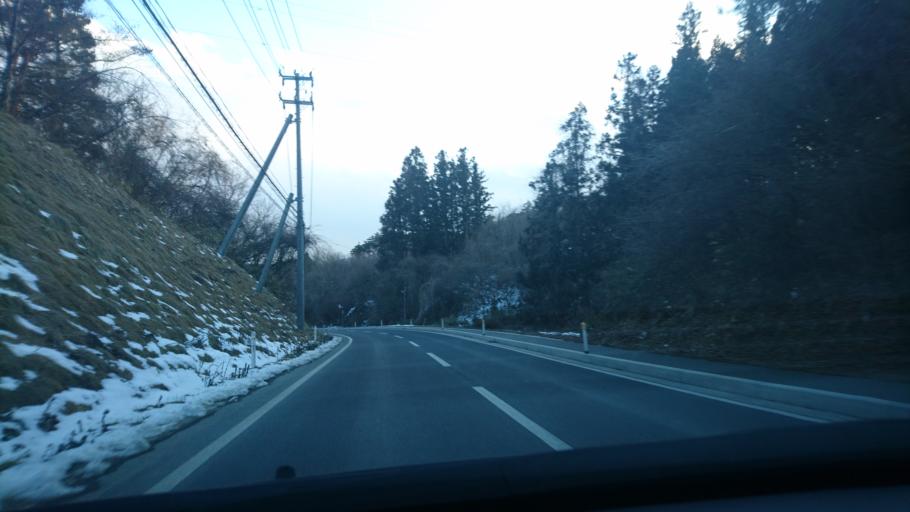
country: JP
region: Iwate
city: Ichinoseki
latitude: 39.0052
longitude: 141.3327
